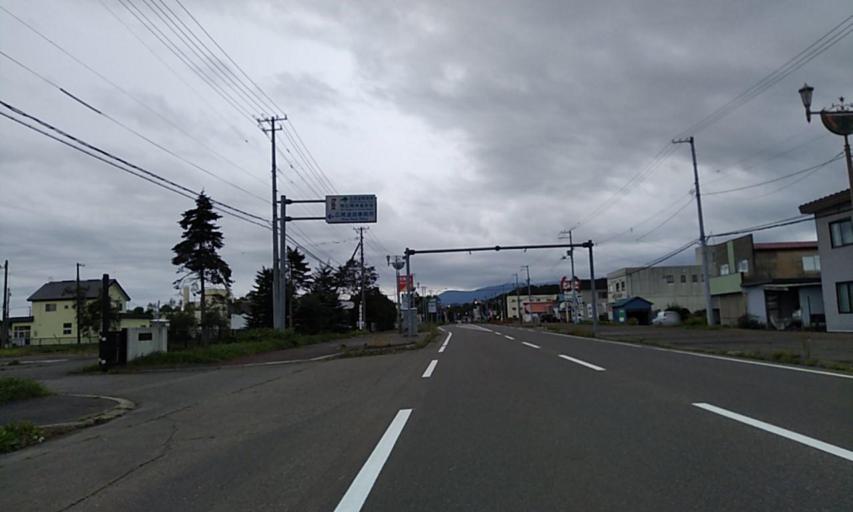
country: JP
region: Hokkaido
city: Obihiro
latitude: 42.2995
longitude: 143.3150
